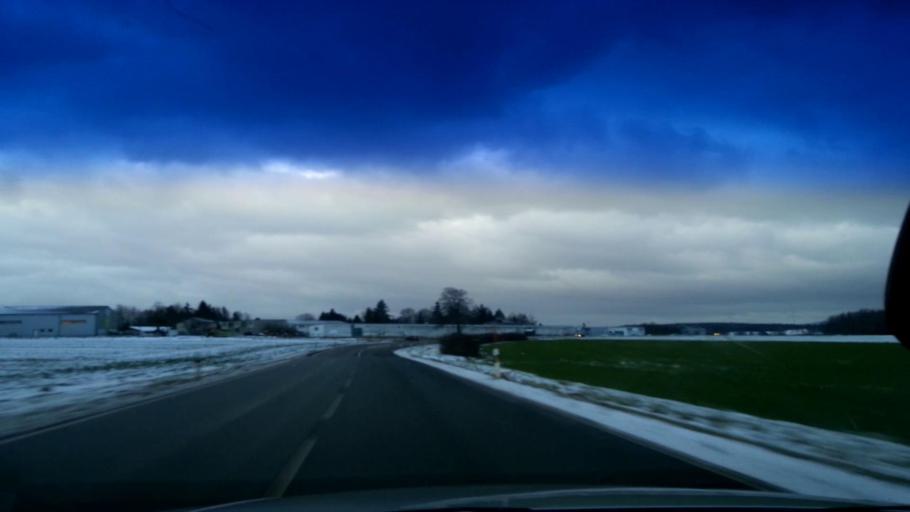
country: DE
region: Bavaria
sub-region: Upper Franconia
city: Marktleuthen
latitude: 50.1390
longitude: 12.0126
